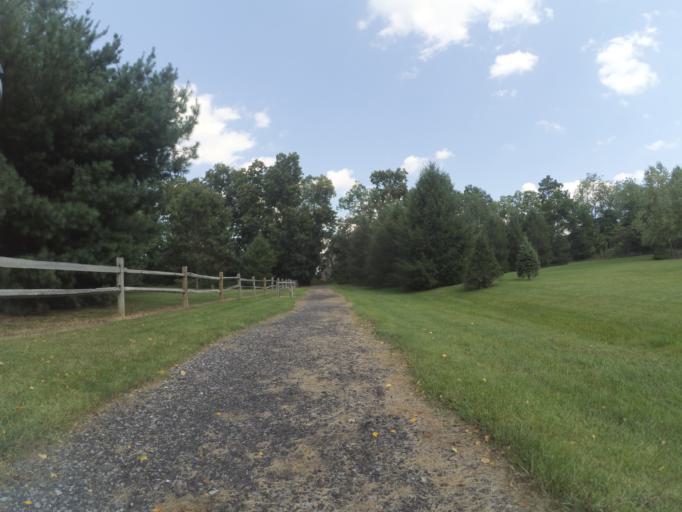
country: US
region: Pennsylvania
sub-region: Centre County
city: Houserville
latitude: 40.8234
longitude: -77.8210
